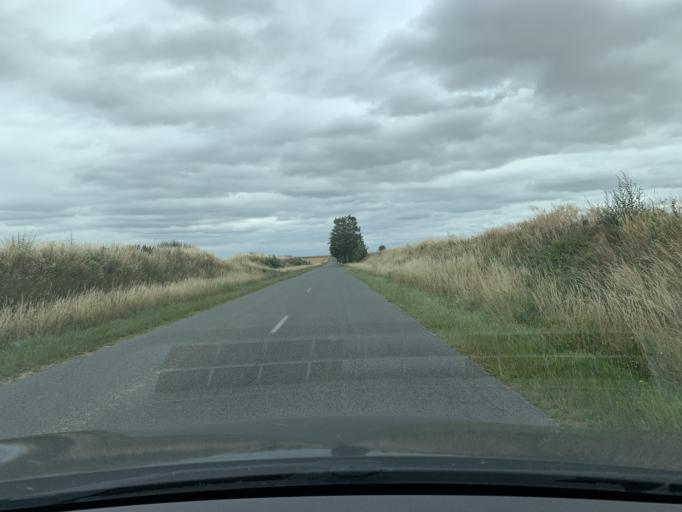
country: FR
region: Nord-Pas-de-Calais
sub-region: Departement du Pas-de-Calais
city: Oisy-le-Verger
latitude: 50.2258
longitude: 3.1362
